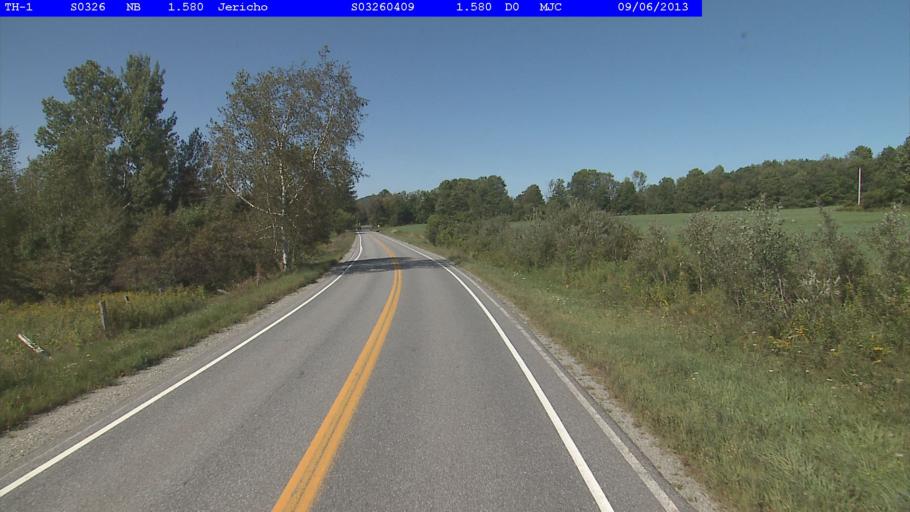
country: US
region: Vermont
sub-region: Chittenden County
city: Jericho
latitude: 44.4994
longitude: -72.9535
